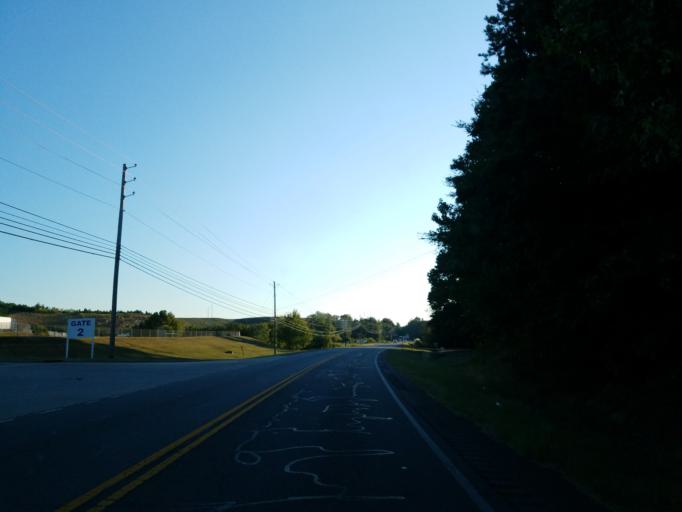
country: US
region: Georgia
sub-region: Bartow County
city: Rydal
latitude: 34.2939
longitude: -84.7345
